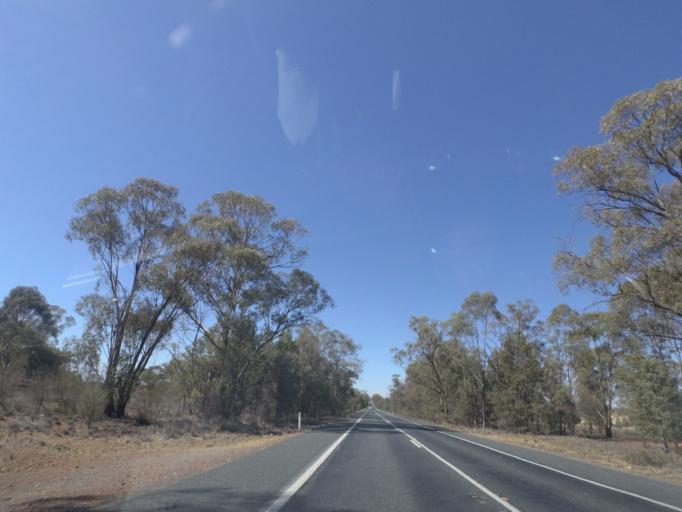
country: AU
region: New South Wales
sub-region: Bland
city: West Wyalong
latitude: -34.1684
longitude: 147.1155
